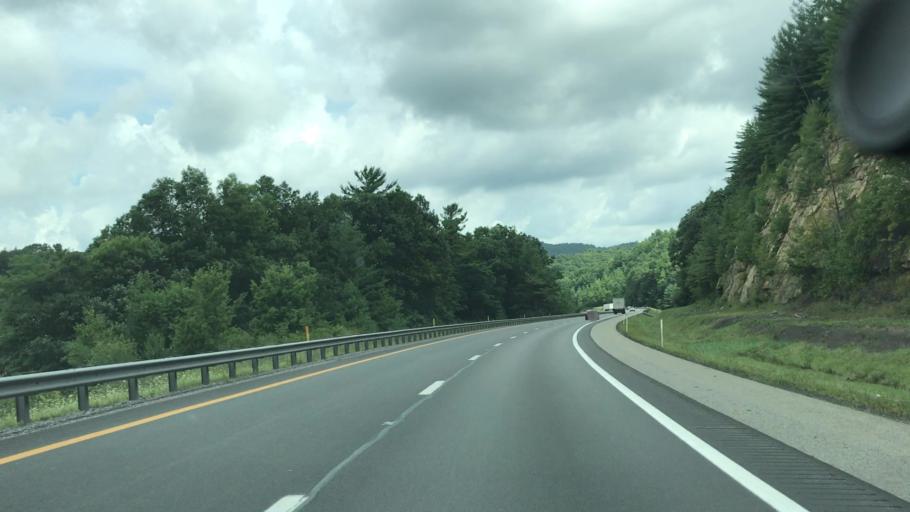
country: US
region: West Virginia
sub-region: Raleigh County
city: Shady Spring
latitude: 37.6660
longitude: -81.1154
